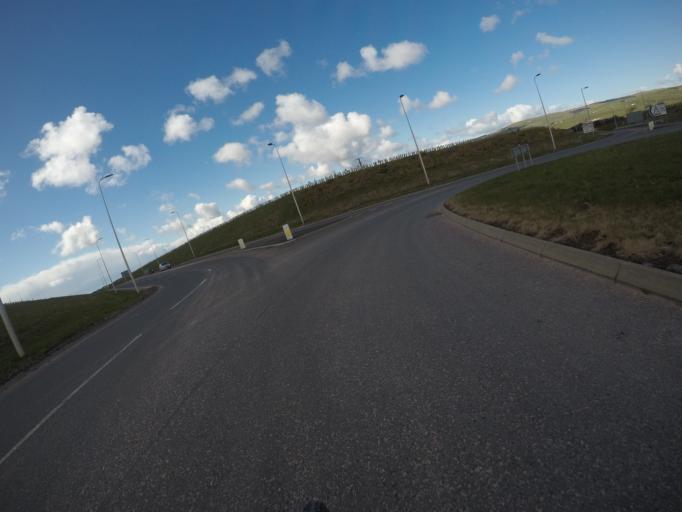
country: GB
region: Scotland
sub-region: North Ayrshire
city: Dalry
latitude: 55.7134
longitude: -4.6939
